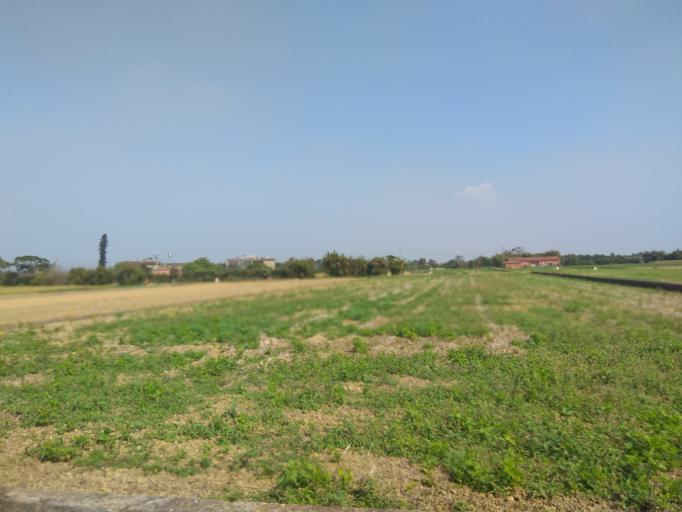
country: TW
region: Taiwan
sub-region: Hsinchu
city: Zhubei
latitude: 24.9942
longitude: 121.0665
